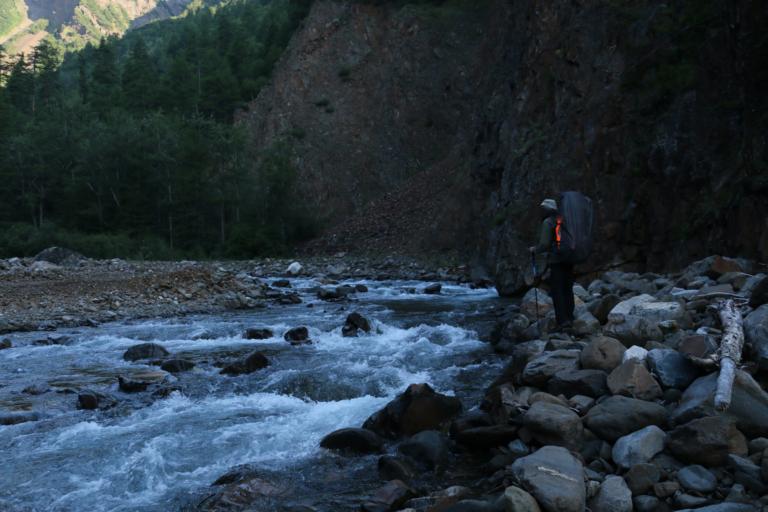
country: RU
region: Respublika Buryatiya
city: Novyy Uoyan
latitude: 56.3003
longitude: 111.3585
